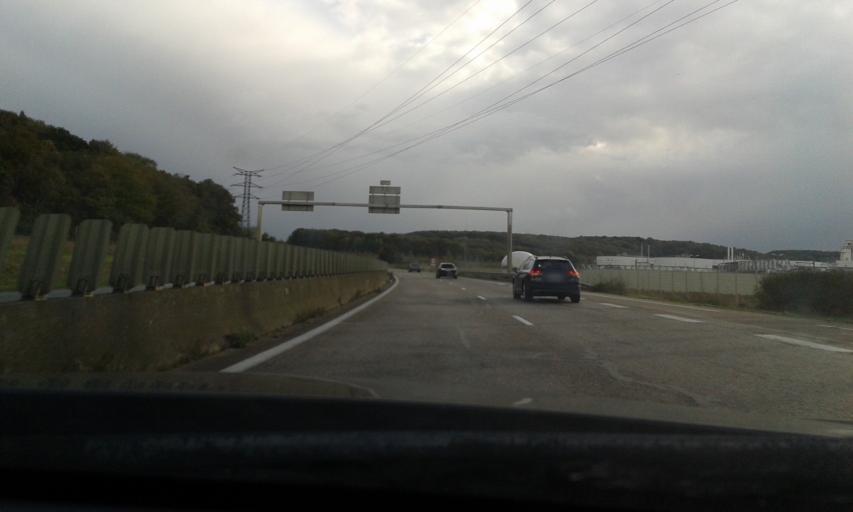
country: FR
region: Haute-Normandie
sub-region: Departement de l'Eure
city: Gravigny
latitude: 49.0571
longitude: 1.1747
